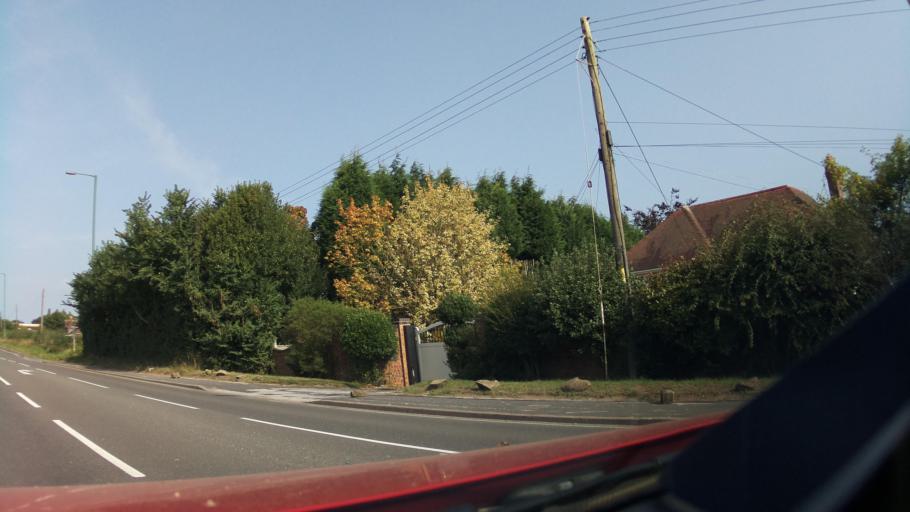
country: GB
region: England
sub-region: Walsall
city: Aldridge
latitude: 52.6221
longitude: -1.8936
